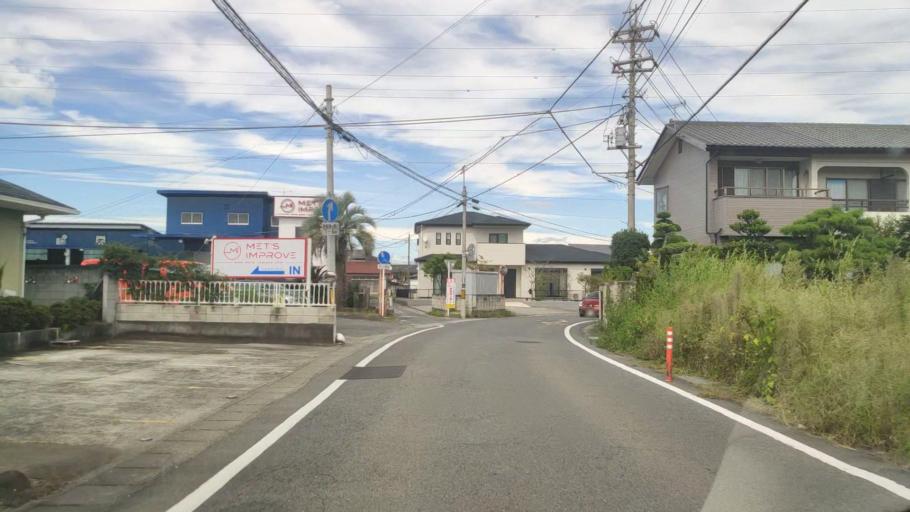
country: JP
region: Gunma
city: Takasaki
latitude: 36.3593
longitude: 139.0055
